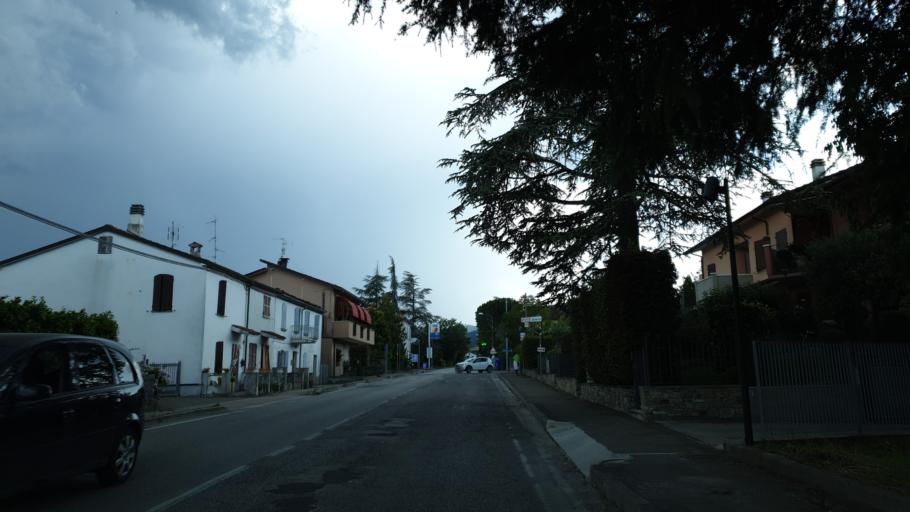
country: IT
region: Emilia-Romagna
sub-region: Provincia di Rimini
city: Secchiano
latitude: 43.9275
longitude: 12.3217
